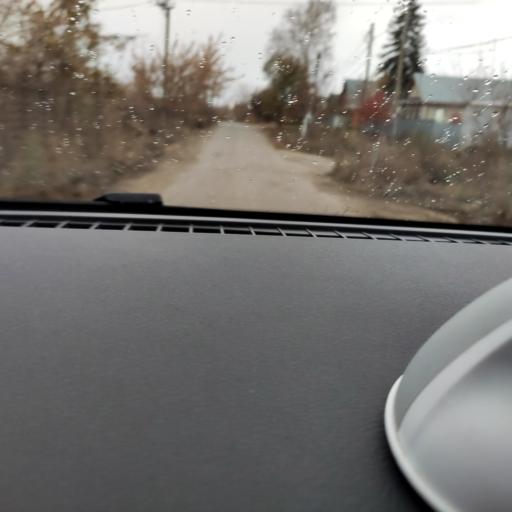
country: RU
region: Samara
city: Petra-Dubrava
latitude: 53.2975
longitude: 50.3041
